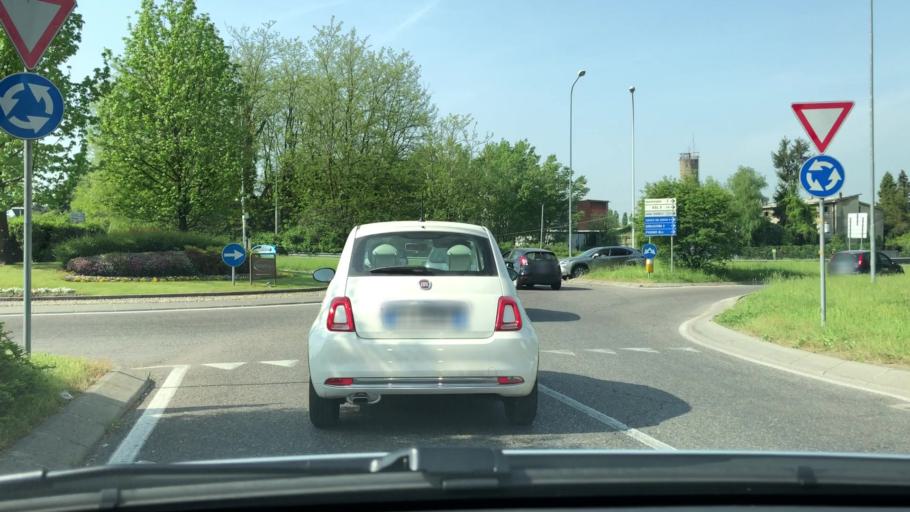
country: IT
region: Lombardy
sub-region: Provincia di Monza e Brianza
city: Meda
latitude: 45.6579
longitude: 9.1556
